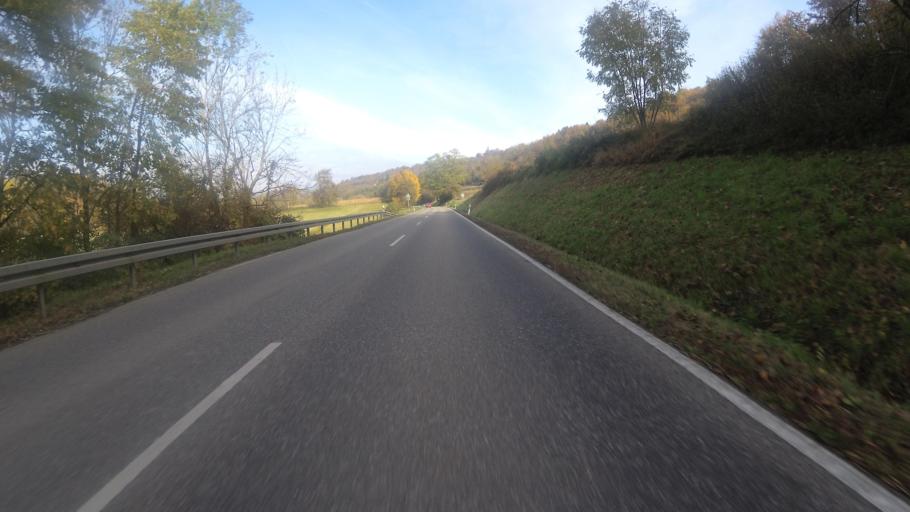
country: DE
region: Baden-Wuerttemberg
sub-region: Regierungsbezirk Stuttgart
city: Mockmuhl
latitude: 49.3054
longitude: 9.3627
